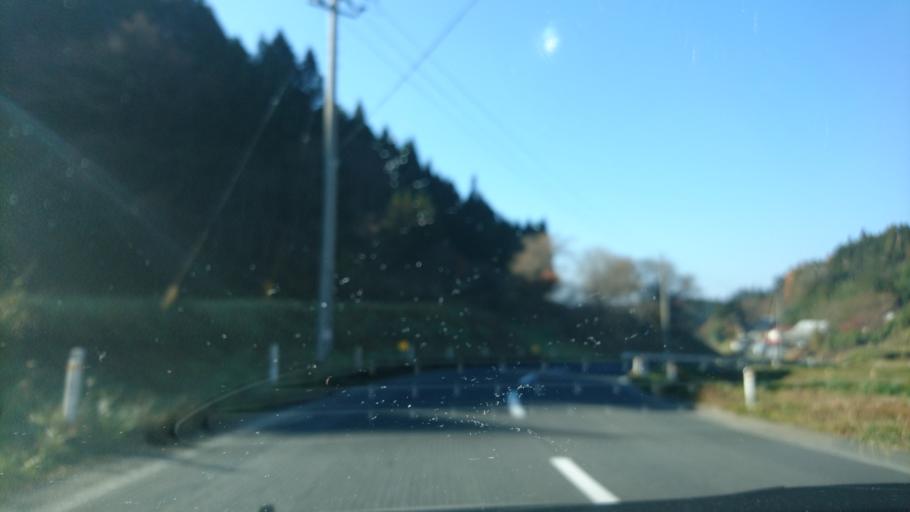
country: JP
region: Iwate
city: Ichinoseki
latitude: 38.9005
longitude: 141.4074
